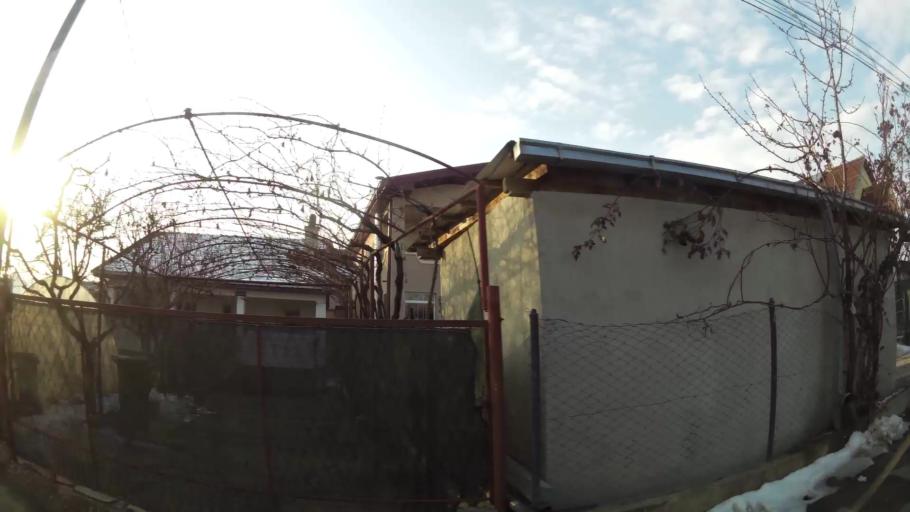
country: MK
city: Creshevo
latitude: 42.0260
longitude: 21.5198
